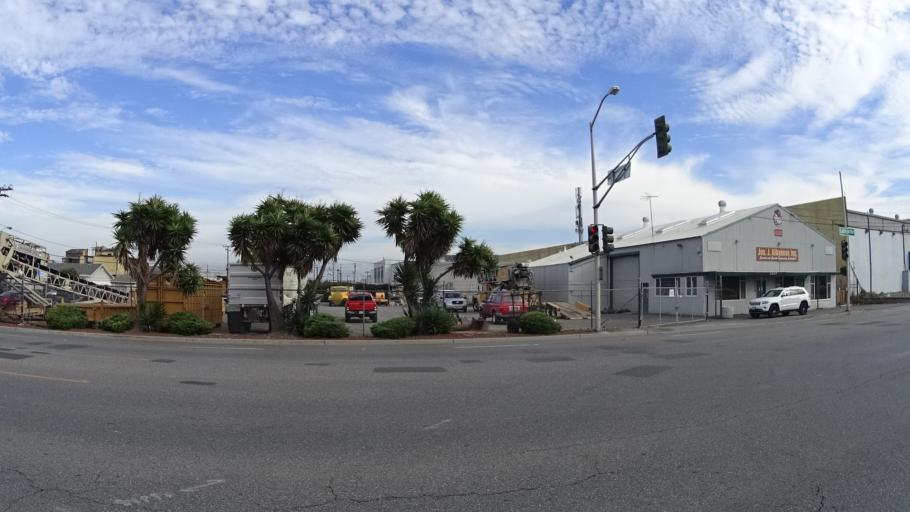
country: US
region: California
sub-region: Santa Clara County
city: Santa Clara
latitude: 37.3627
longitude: -121.9491
